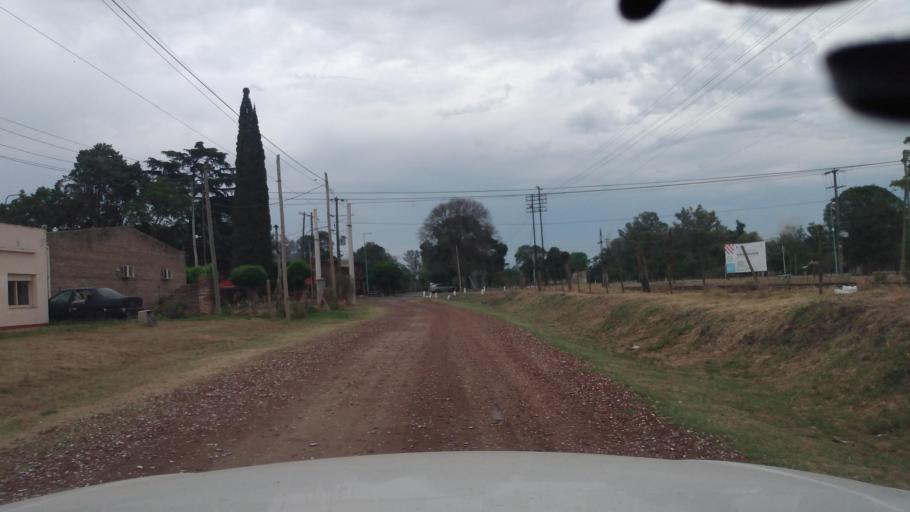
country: AR
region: Buenos Aires
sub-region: Partido de Lujan
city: Lujan
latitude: -34.5546
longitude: -59.2044
